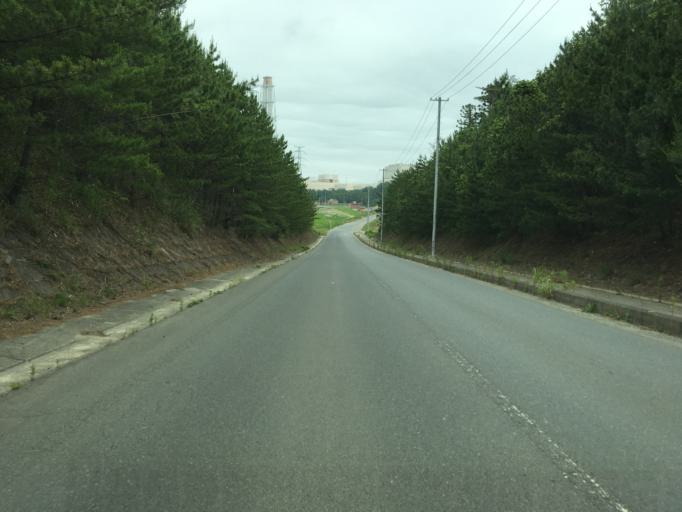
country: JP
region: Fukushima
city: Namie
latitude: 37.6564
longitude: 141.0139
